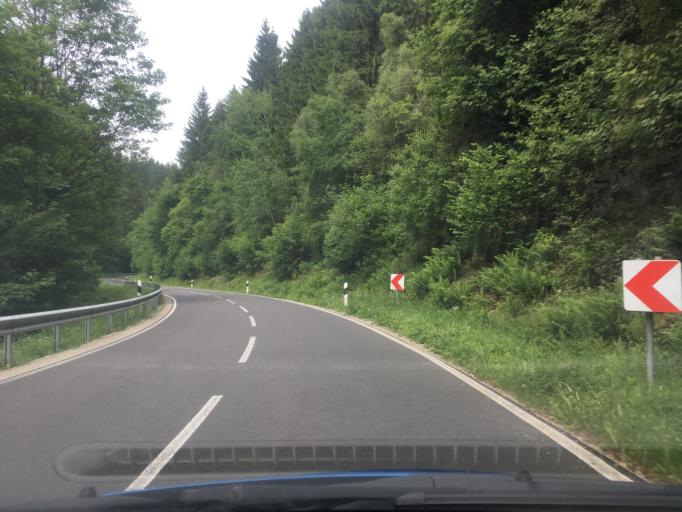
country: DE
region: Lower Saxony
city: Dassel
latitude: 51.7464
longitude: 9.6583
